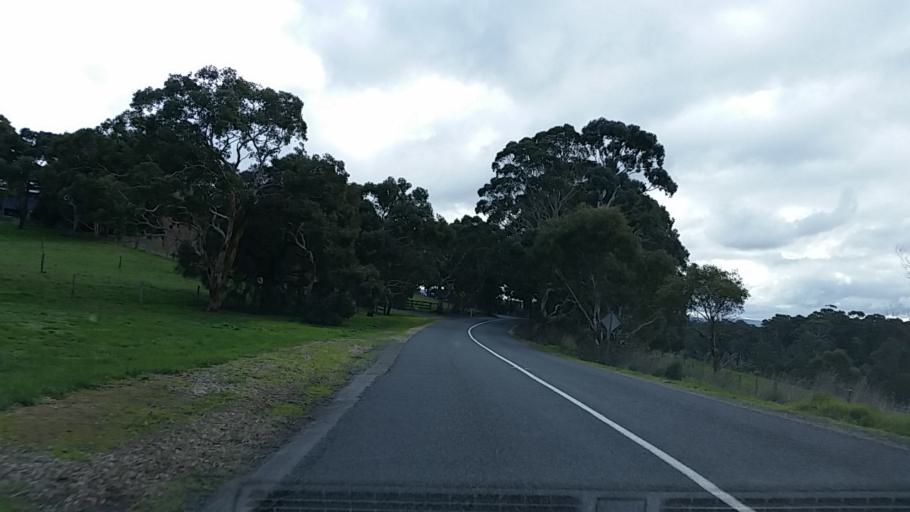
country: AU
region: South Australia
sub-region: Mount Barker
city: Little Hampton
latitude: -35.0771
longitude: 138.8196
